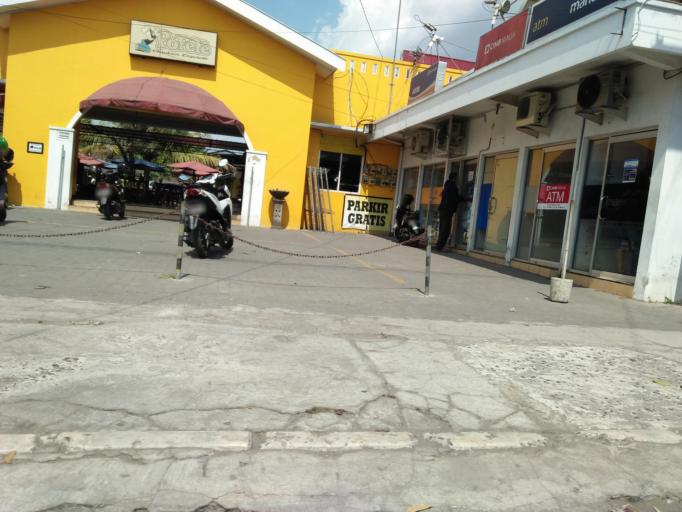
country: ID
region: Daerah Istimewa Yogyakarta
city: Kasihan
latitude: -7.8201
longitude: 110.3556
